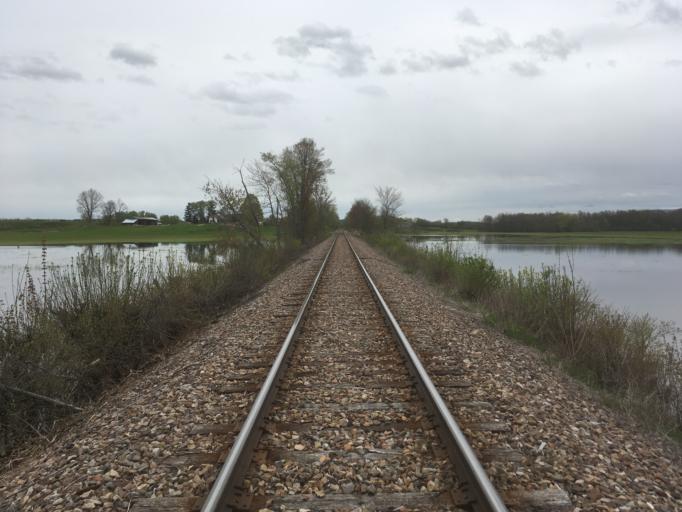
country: US
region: Vermont
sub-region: Addison County
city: Middlebury (village)
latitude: 43.9603
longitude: -73.1624
